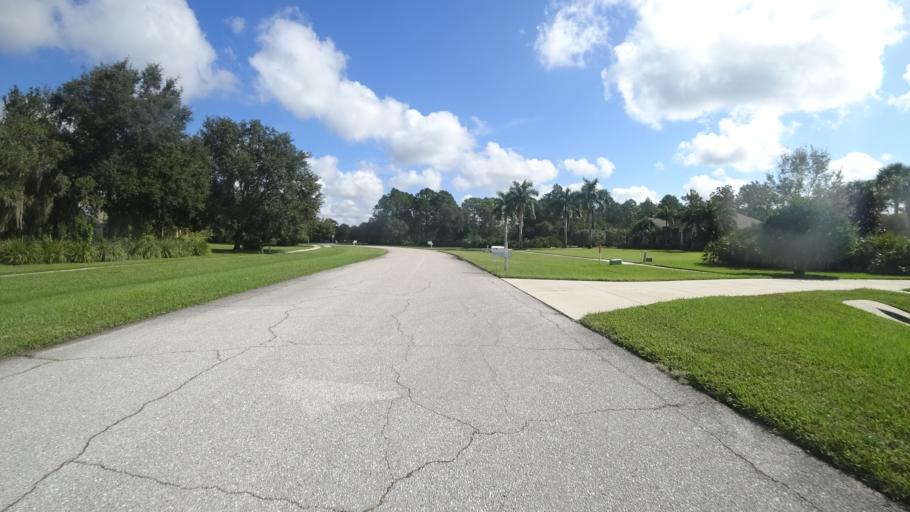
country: US
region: Florida
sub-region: Sarasota County
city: The Meadows
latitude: 27.3994
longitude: -82.3200
